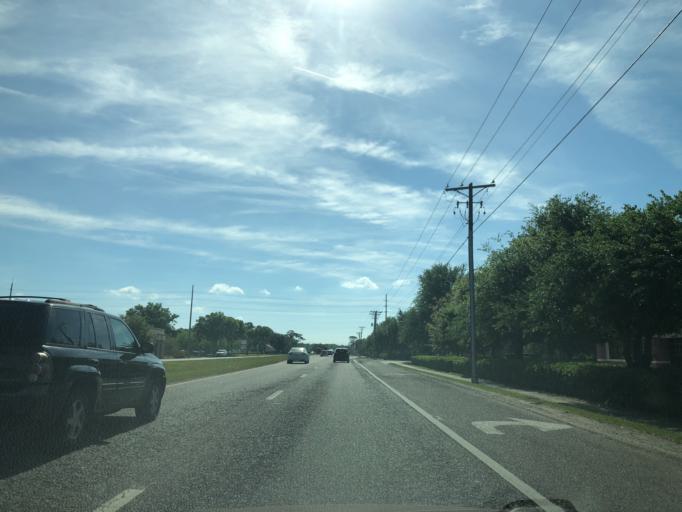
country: US
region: Florida
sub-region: Orange County
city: Apopka
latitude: 28.6879
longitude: -81.5404
